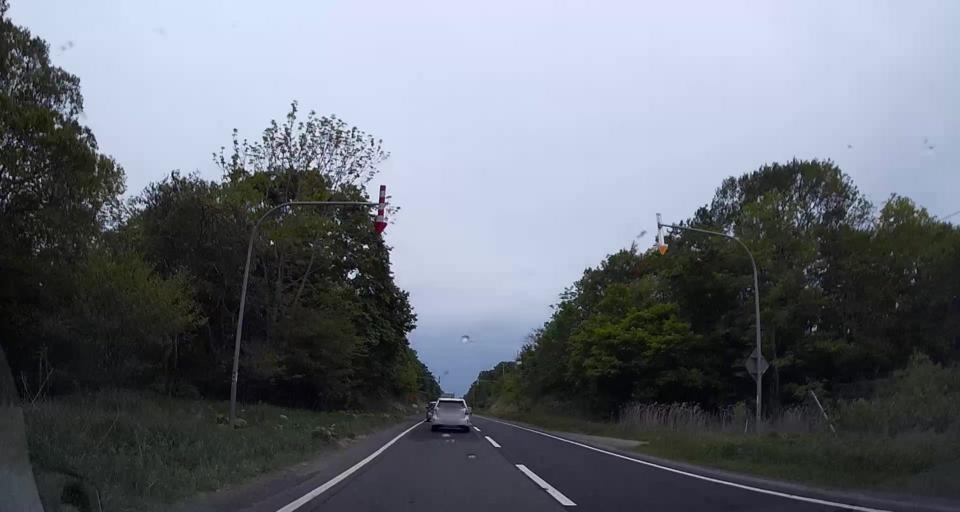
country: JP
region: Hokkaido
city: Chitose
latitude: 42.7064
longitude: 141.7442
